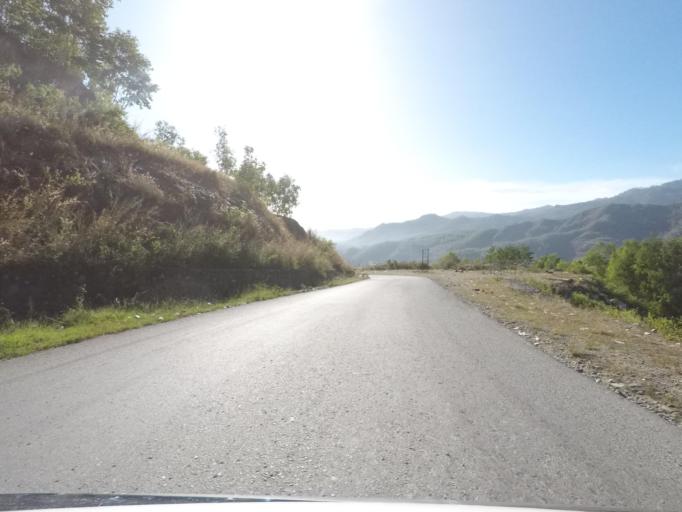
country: TL
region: Dili
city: Dili
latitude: -8.5613
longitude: 125.6388
